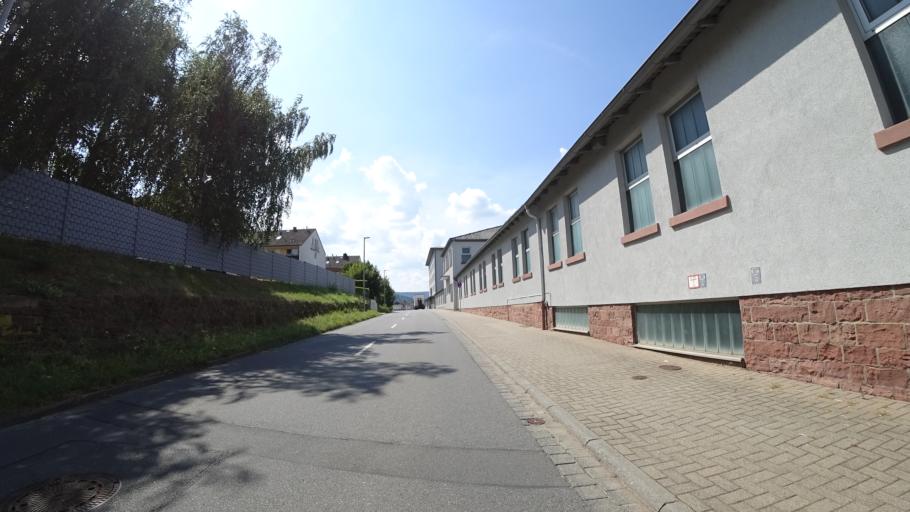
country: DE
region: Bavaria
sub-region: Regierungsbezirk Unterfranken
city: Miltenberg
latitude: 49.7054
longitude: 9.2743
